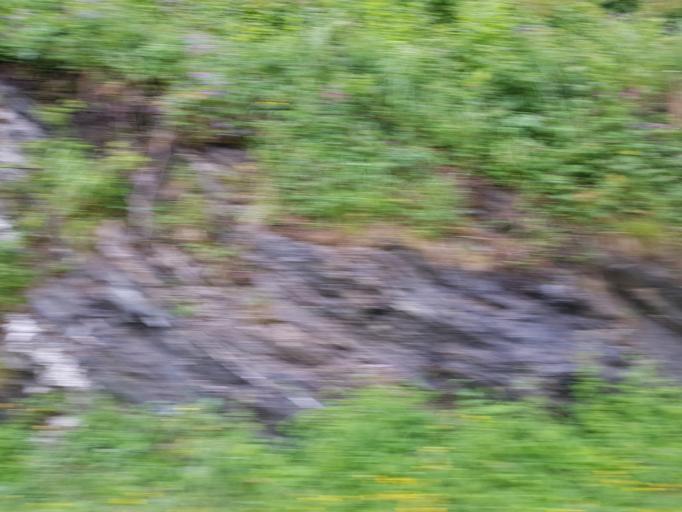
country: NO
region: Sor-Trondelag
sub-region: Selbu
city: Mebonden
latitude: 63.3122
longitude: 11.0810
